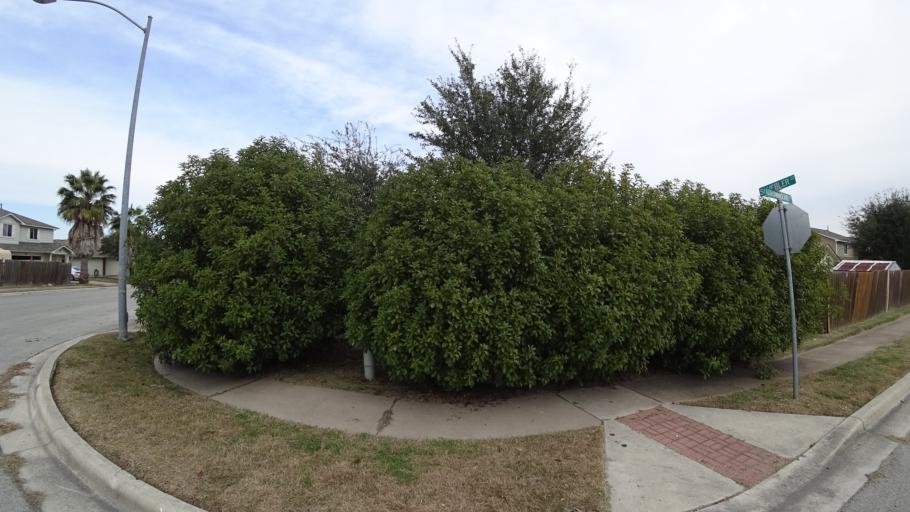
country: US
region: Texas
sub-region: Travis County
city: Garfield
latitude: 30.1545
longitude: -97.6505
